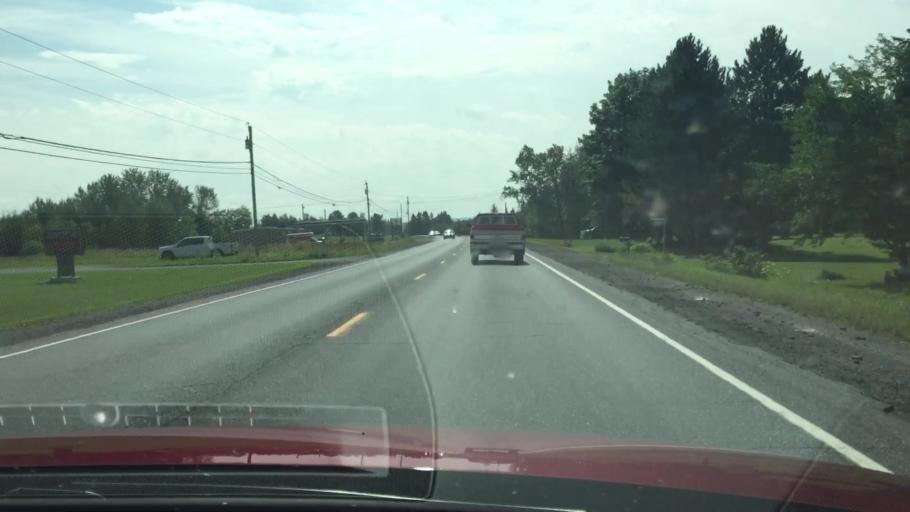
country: US
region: Maine
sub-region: Aroostook County
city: Easton
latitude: 46.6136
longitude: -67.9802
